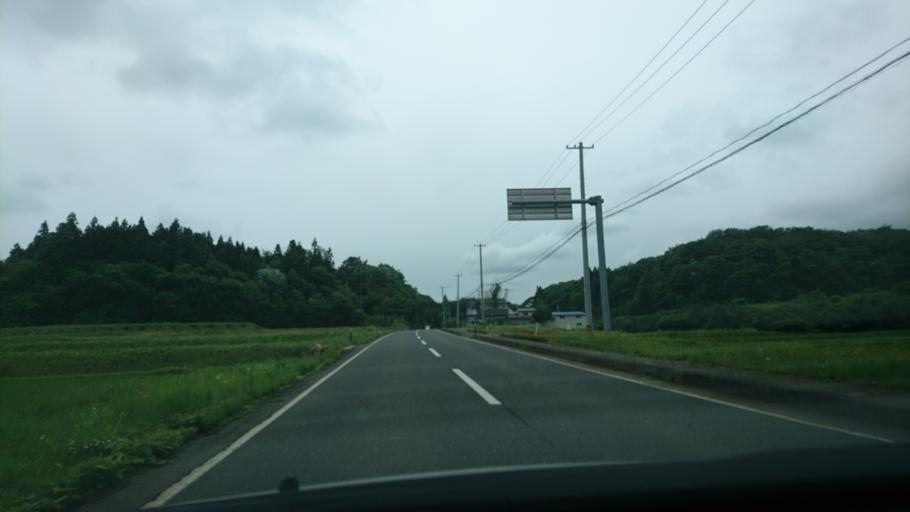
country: JP
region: Iwate
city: Ichinoseki
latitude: 38.9668
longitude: 141.0581
